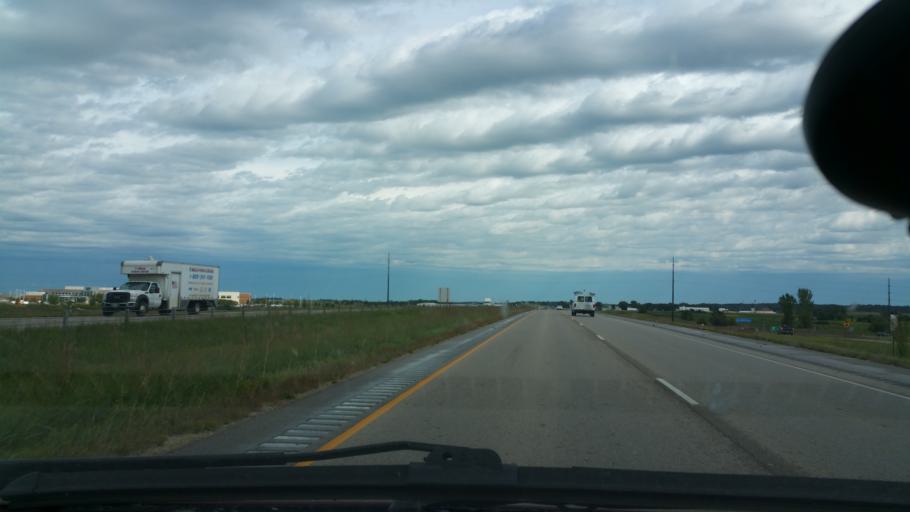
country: US
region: Minnesota
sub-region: Steele County
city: Owatonna
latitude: 44.1066
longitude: -93.2457
